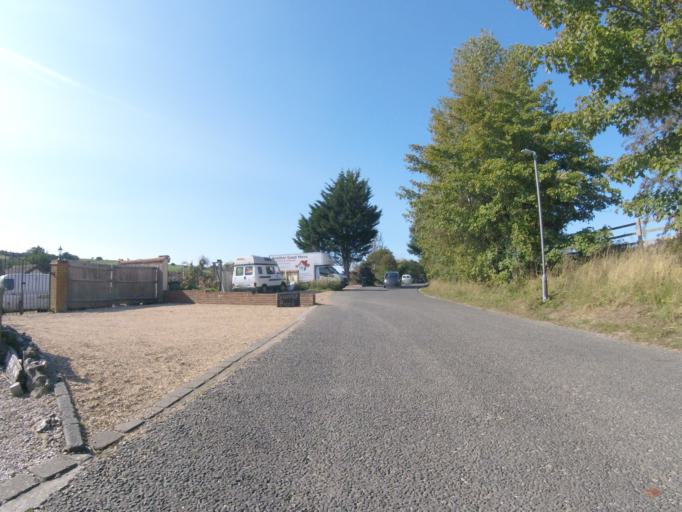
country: GB
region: England
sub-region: Brighton and Hove
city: Hove
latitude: 50.8704
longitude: -0.1572
